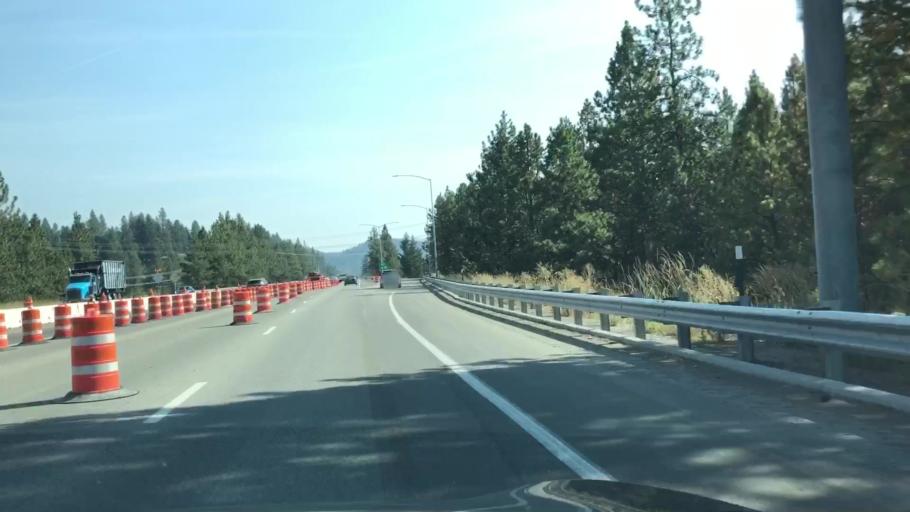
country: US
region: Idaho
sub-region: Kootenai County
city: Coeur d'Alene
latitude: 47.6915
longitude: -116.7678
